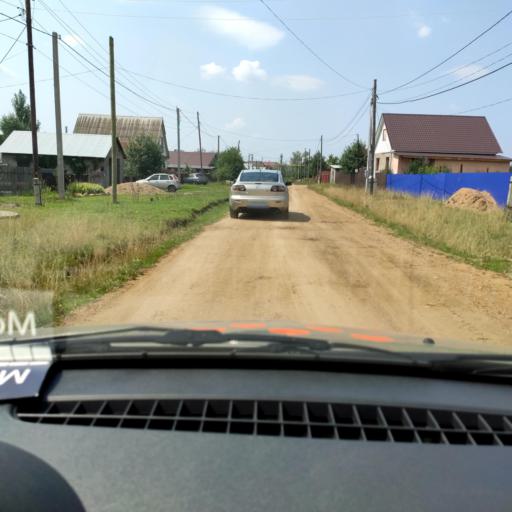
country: RU
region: Bashkortostan
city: Iglino
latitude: 54.8071
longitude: 56.4094
